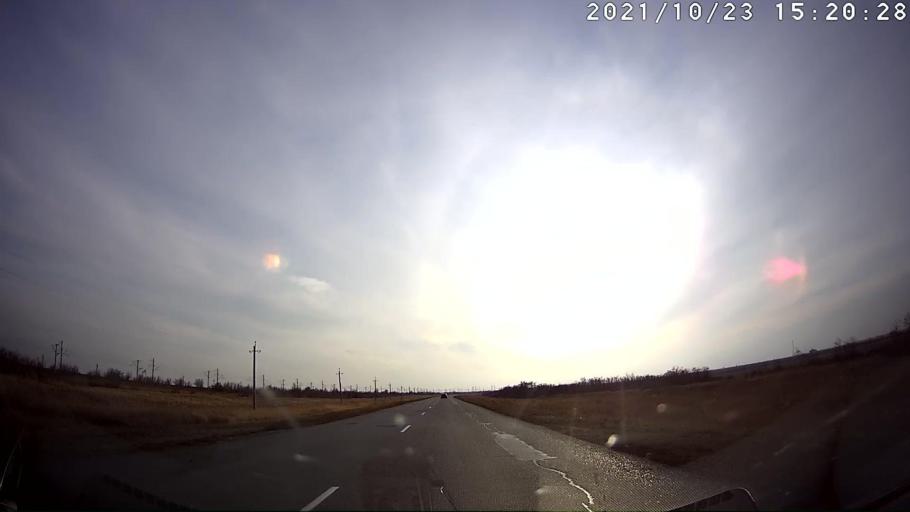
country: RU
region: Volgograd
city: Bereslavka
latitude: 48.3212
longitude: 44.3259
